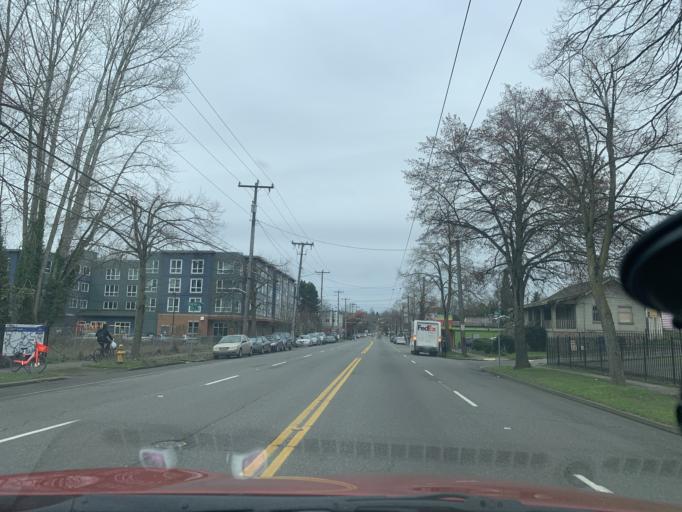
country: US
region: Washington
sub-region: King County
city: Bryn Mawr-Skyway
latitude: 47.5307
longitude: -122.2701
